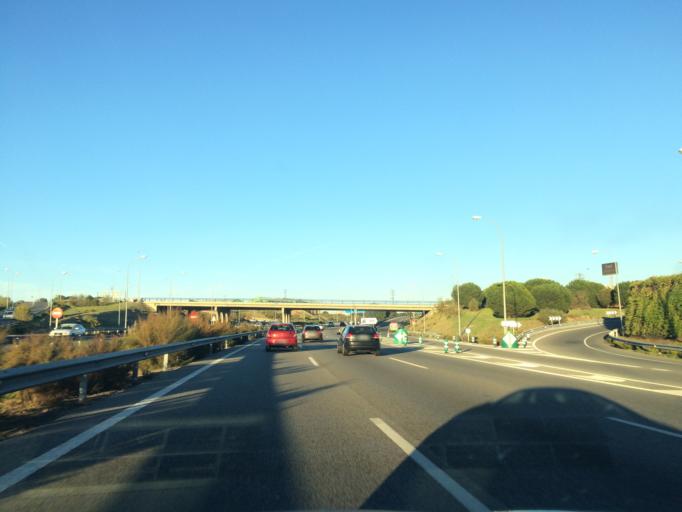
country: ES
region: Madrid
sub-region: Provincia de Madrid
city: Pozuelo de Alarcon
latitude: 40.4568
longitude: -3.8147
